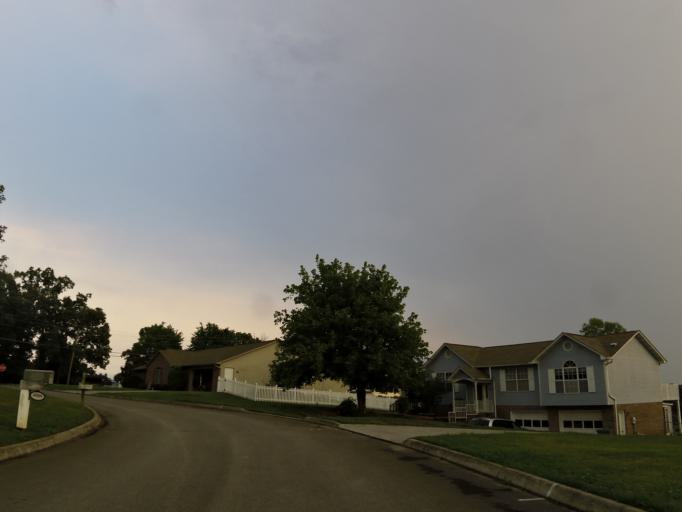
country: US
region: Tennessee
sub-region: Blount County
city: Wildwood
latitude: 35.8023
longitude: -83.8845
